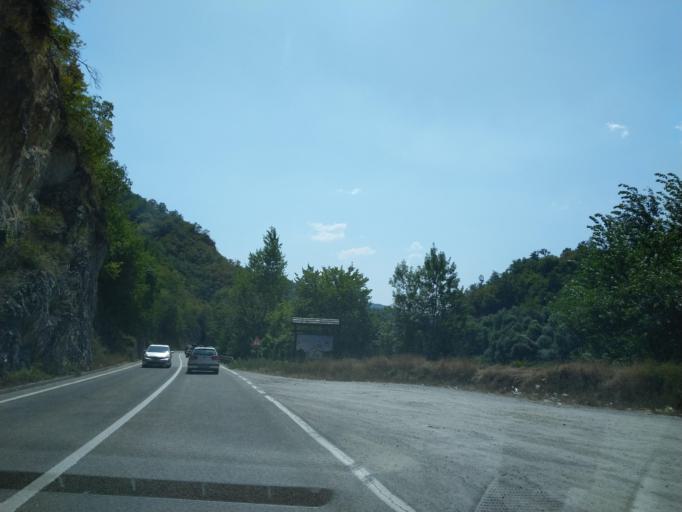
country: RS
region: Central Serbia
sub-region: Zlatiborski Okrug
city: Prijepolje
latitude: 43.4543
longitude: 19.6424
